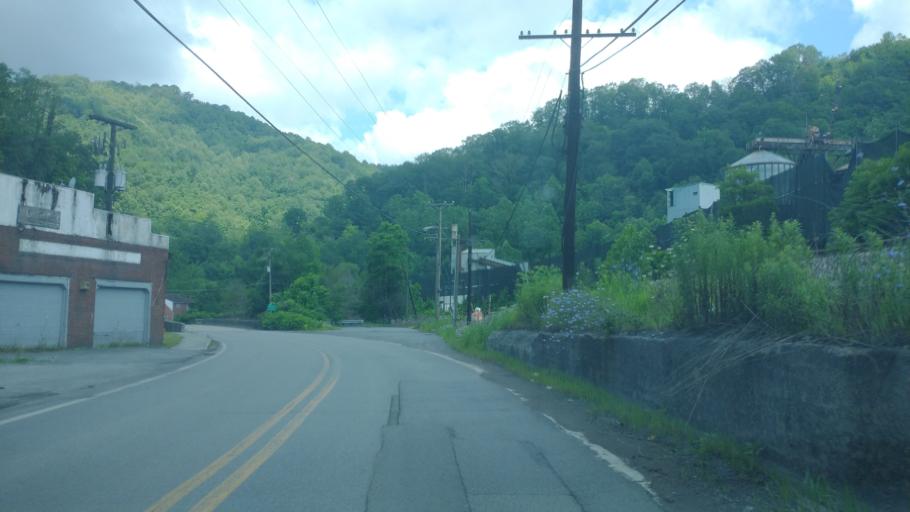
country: US
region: West Virginia
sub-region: McDowell County
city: Welch
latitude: 37.4159
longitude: -81.4475
